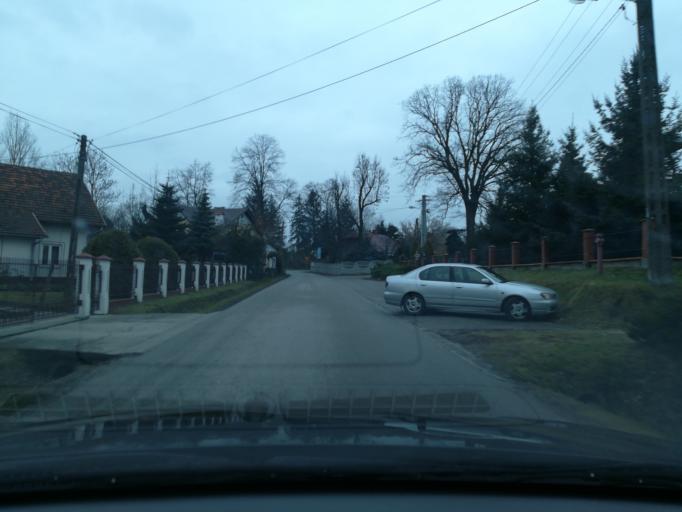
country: PL
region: Subcarpathian Voivodeship
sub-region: Powiat lancucki
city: Gluchow
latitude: 50.0813
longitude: 22.2672
